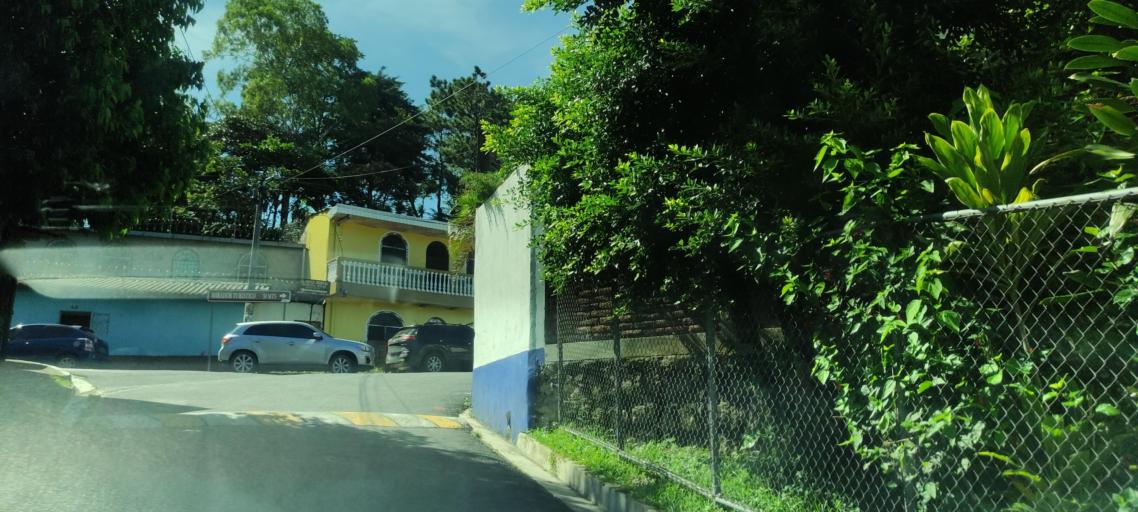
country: HN
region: Ocotepeque
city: Antigua Ocotepeque
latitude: 14.3154
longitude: -89.1697
